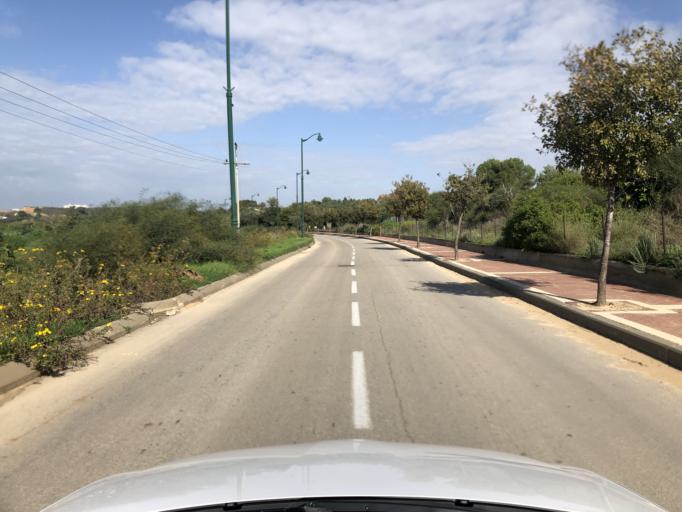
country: IL
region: Central District
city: Ness Ziona
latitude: 31.9127
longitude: 34.7831
